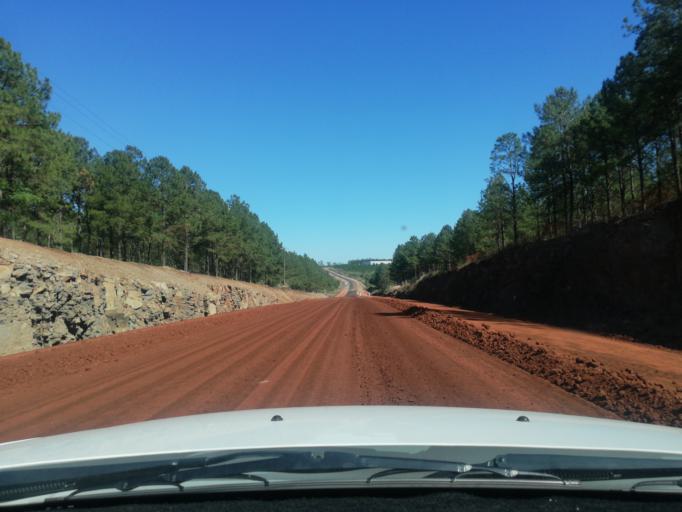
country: AR
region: Misiones
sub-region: Departamento de Candelaria
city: Candelaria
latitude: -27.5175
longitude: -55.7291
